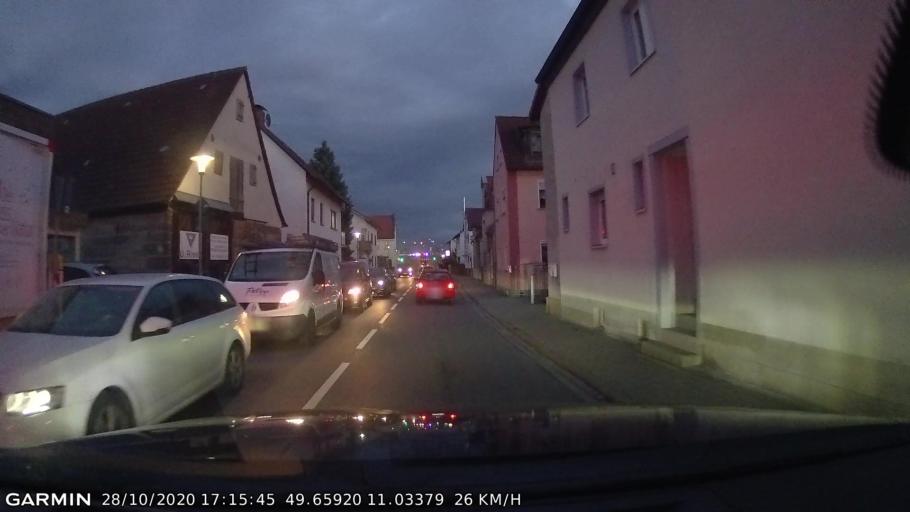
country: DE
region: Bavaria
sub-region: Regierungsbezirk Mittelfranken
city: Baiersdorf
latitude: 49.6593
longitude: 11.0337
